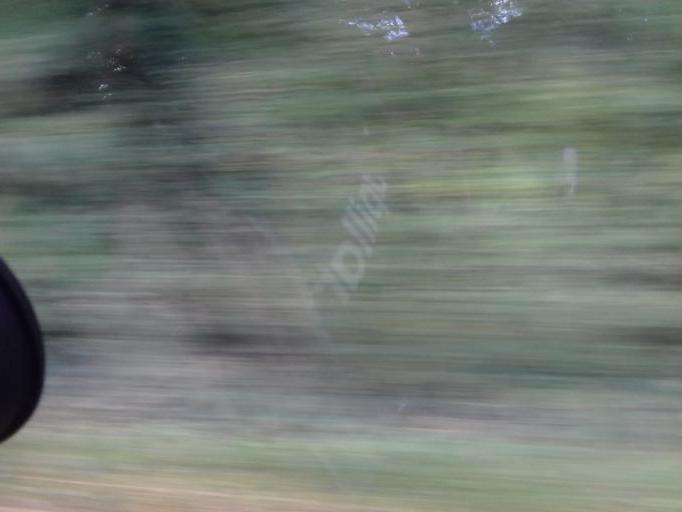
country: IE
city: Kentstown
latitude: 53.6318
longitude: -6.4928
